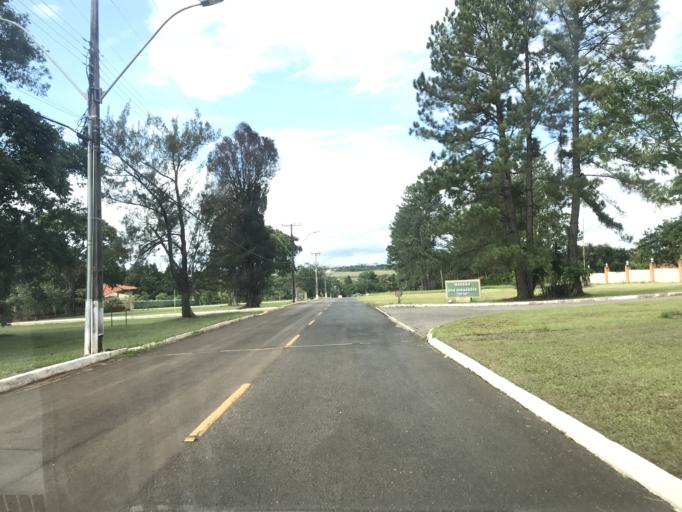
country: BR
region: Federal District
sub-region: Brasilia
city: Brasilia
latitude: -15.8892
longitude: -47.9179
